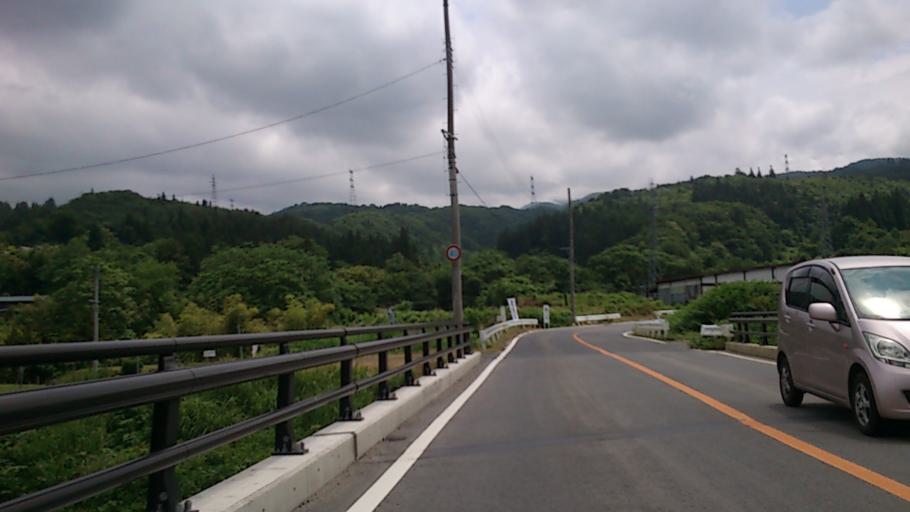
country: JP
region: Yamagata
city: Kaminoyama
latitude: 38.1503
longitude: 140.3296
